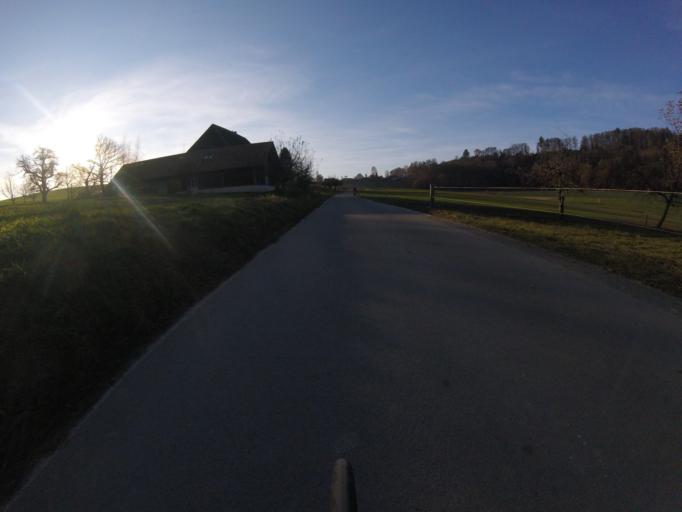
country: CH
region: Bern
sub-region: Bern-Mittelland District
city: Muhleberg
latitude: 46.9382
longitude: 7.2935
